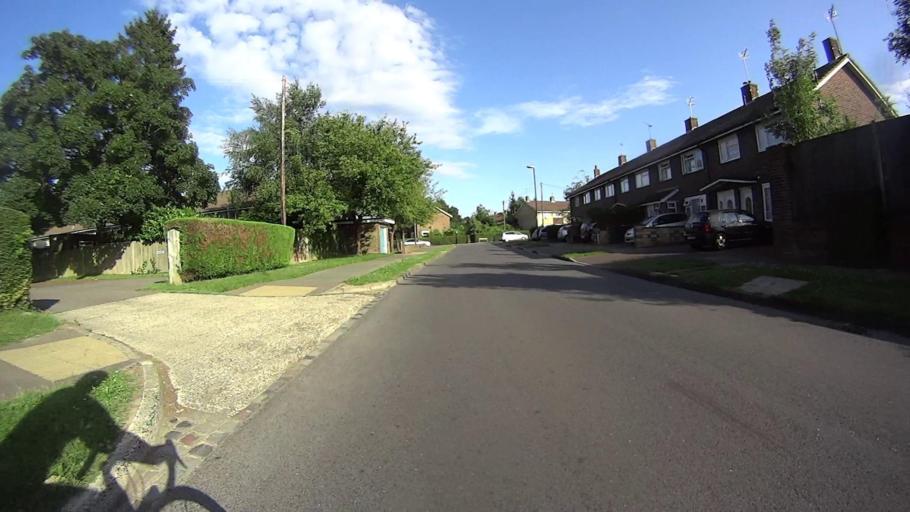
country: GB
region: England
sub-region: West Sussex
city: Crawley
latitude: 51.1079
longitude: -0.1853
